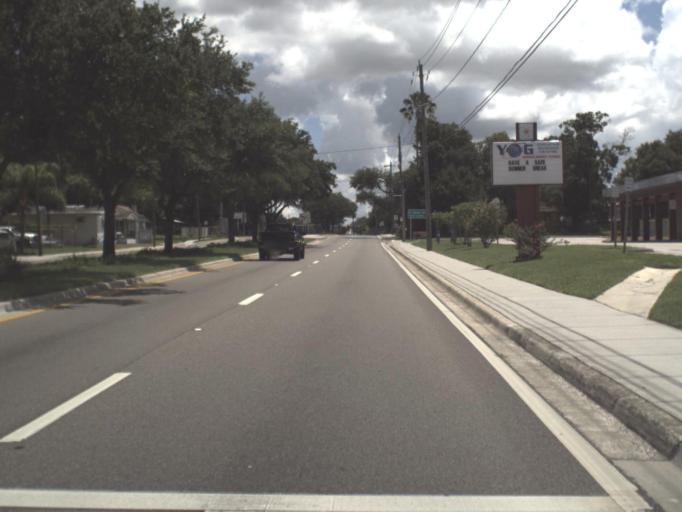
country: US
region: Florida
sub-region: Hillsborough County
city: Tampa
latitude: 27.9814
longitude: -82.4388
